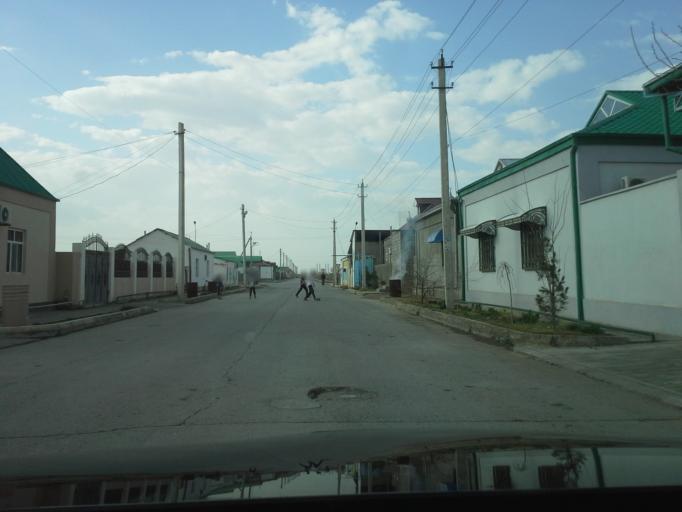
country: TM
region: Ahal
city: Ashgabat
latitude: 37.9917
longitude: 58.2922
